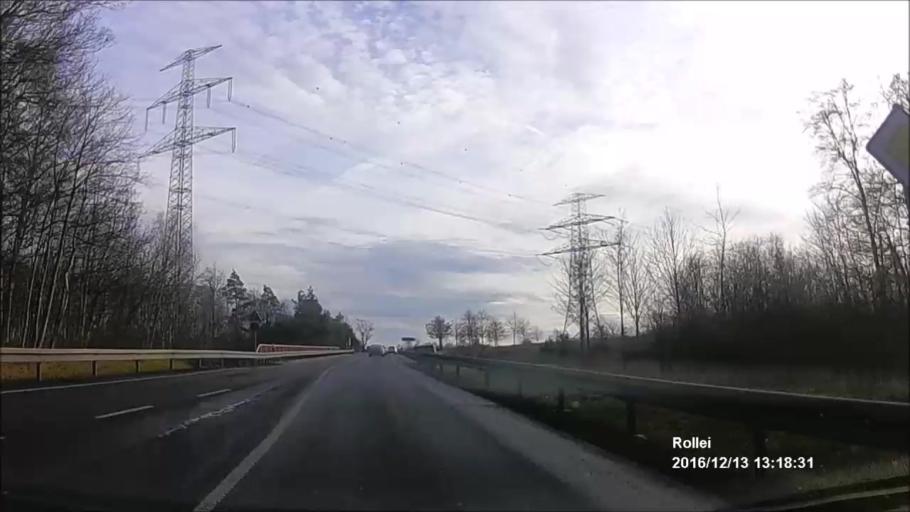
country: DE
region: Thuringia
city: Klettbach
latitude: 50.9274
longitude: 11.1382
